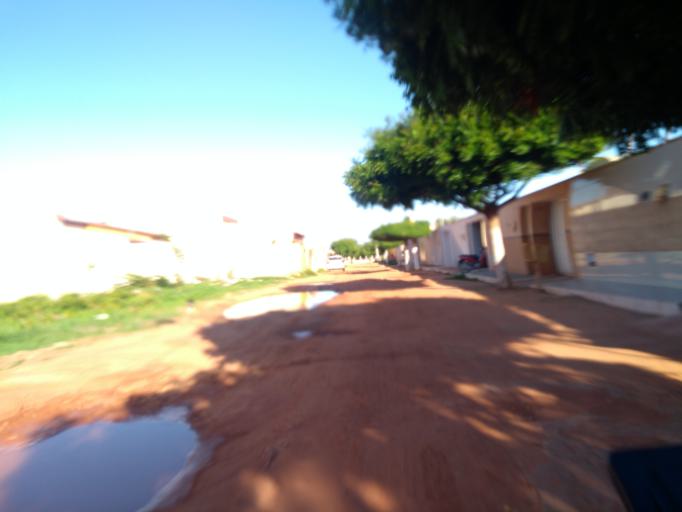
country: BR
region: Ceara
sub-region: Aracati
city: Aracati
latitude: -4.5714
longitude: -37.7956
